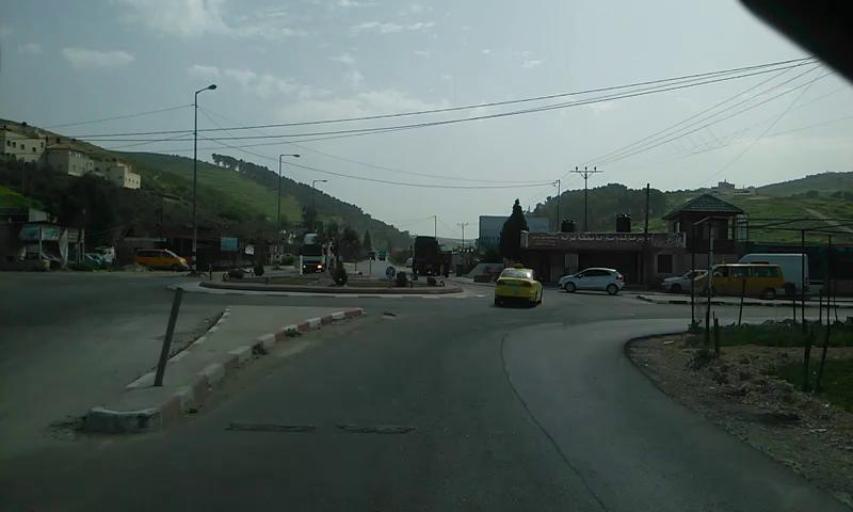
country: PS
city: Bir al Basha
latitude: 32.4082
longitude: 35.2272
